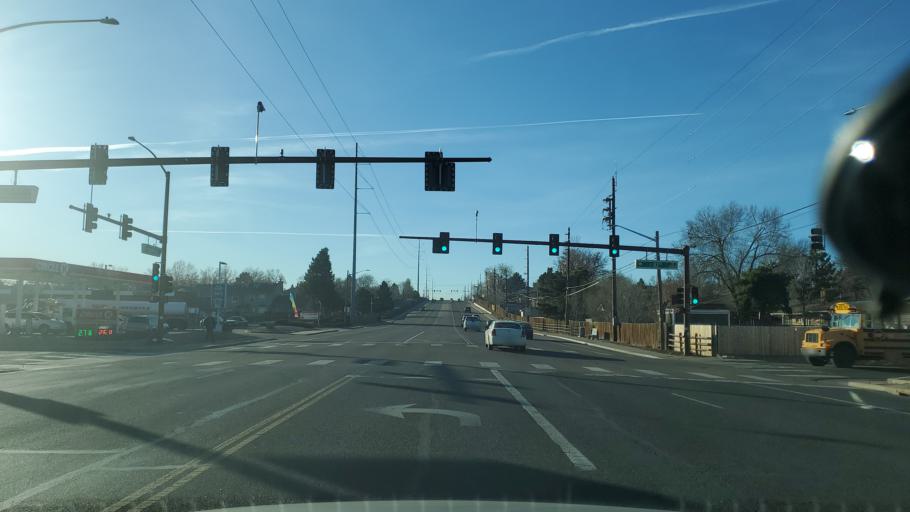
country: US
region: Colorado
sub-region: Adams County
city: Federal Heights
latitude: 39.8469
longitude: -104.9779
